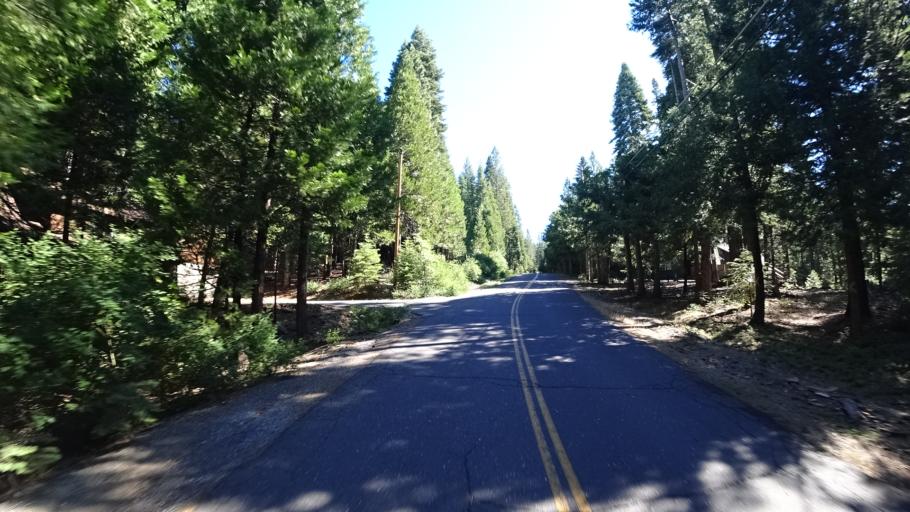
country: US
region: California
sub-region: Calaveras County
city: Arnold
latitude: 38.2920
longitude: -120.2687
